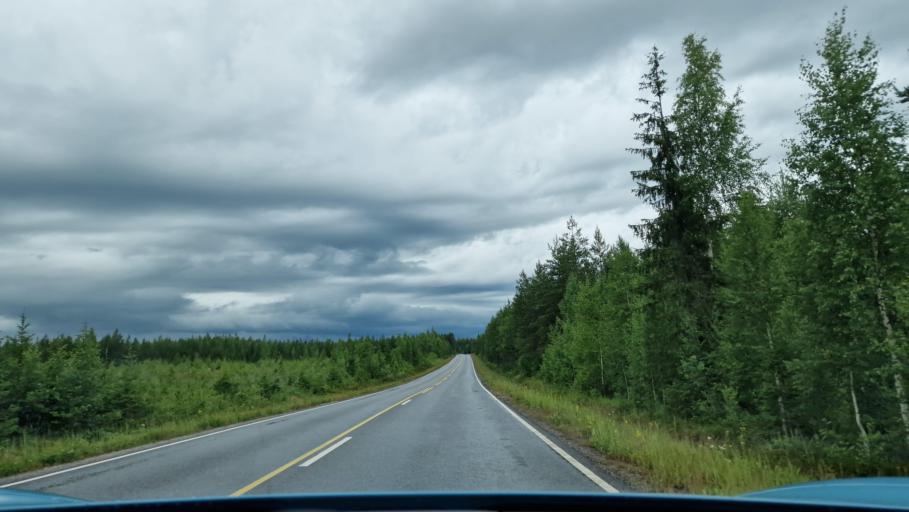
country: FI
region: Southern Ostrobothnia
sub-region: Jaerviseutu
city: Soini
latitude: 62.7115
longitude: 24.4411
